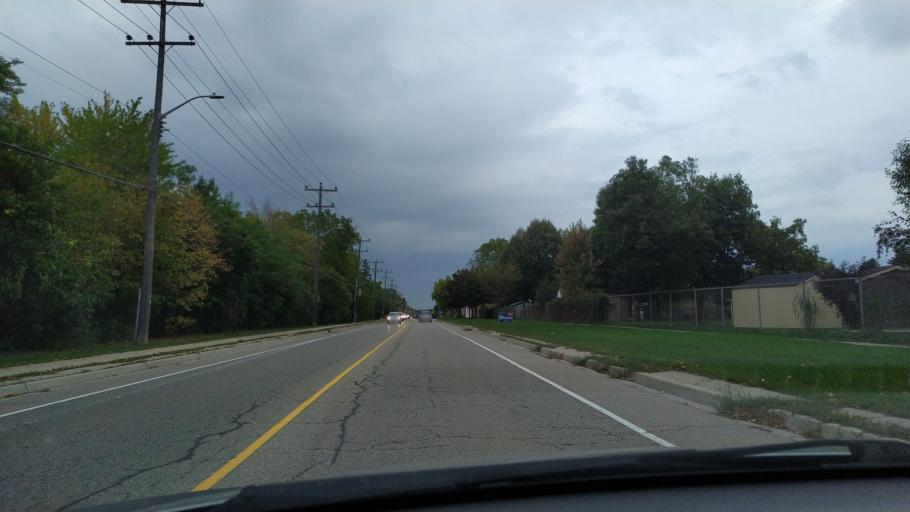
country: CA
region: Ontario
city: Waterloo
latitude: 43.4937
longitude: -80.4989
